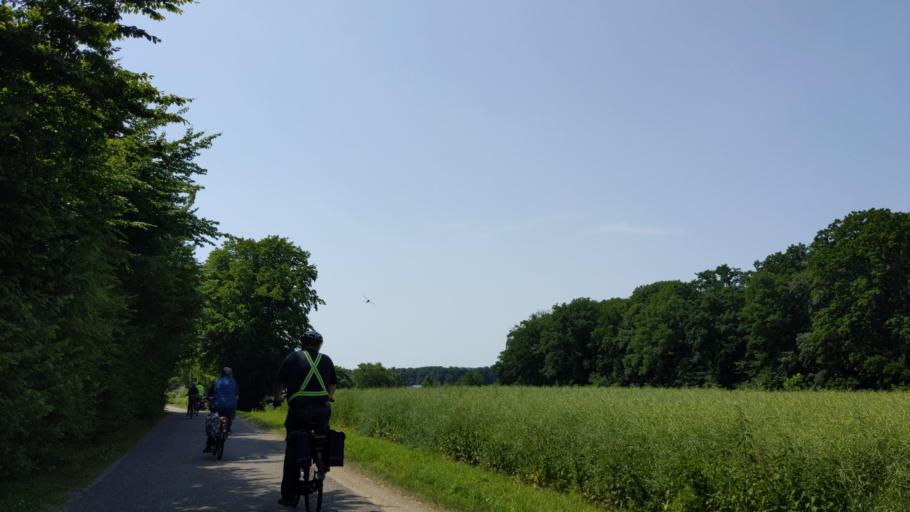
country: DE
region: Schleswig-Holstein
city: Albsfelde
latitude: 53.6863
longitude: 10.7017
